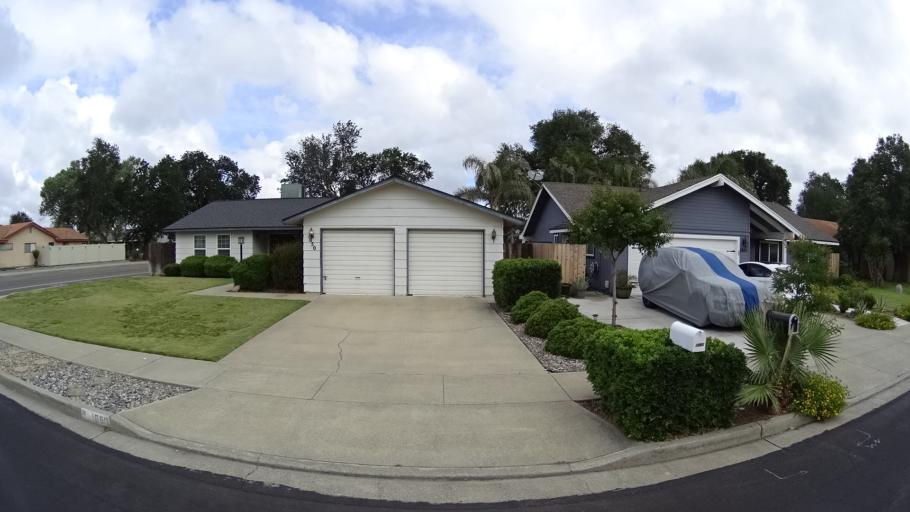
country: US
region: California
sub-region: Kings County
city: Hanford
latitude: 36.3482
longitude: -119.6604
